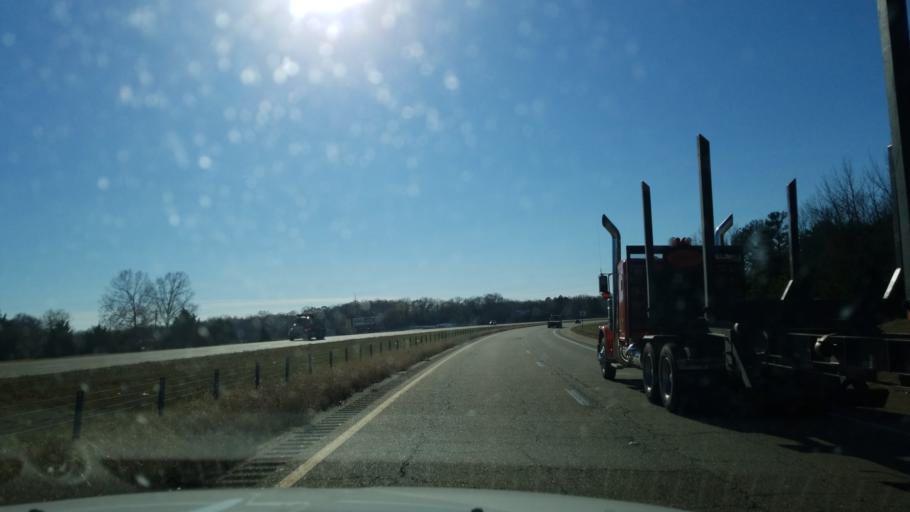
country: US
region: Mississippi
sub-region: Oktibbeha County
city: Starkville
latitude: 33.4728
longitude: -88.7278
